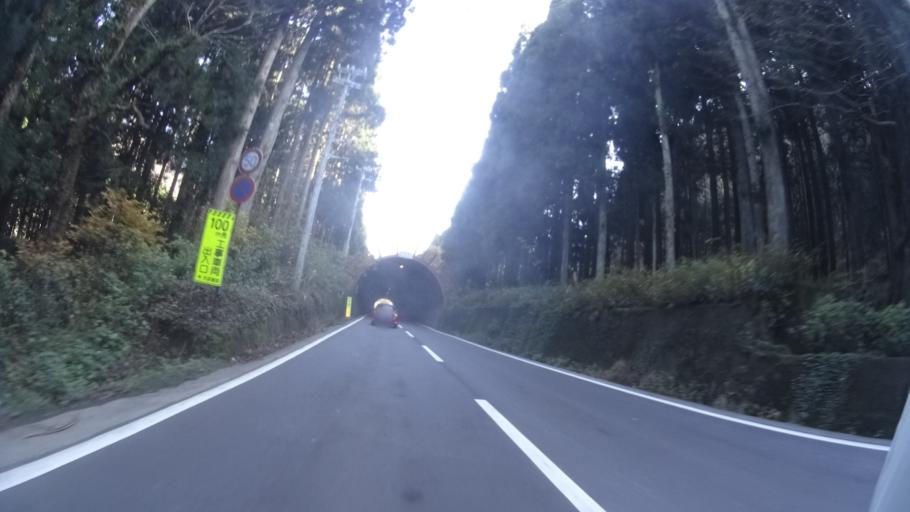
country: JP
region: Fukui
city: Ono
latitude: 35.9663
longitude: 136.5968
